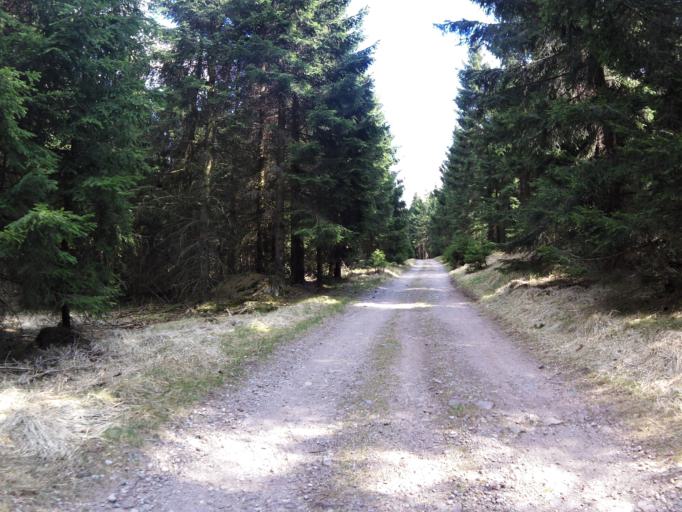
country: DE
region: Thuringia
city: Bermbach
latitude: 50.7170
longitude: 10.6480
